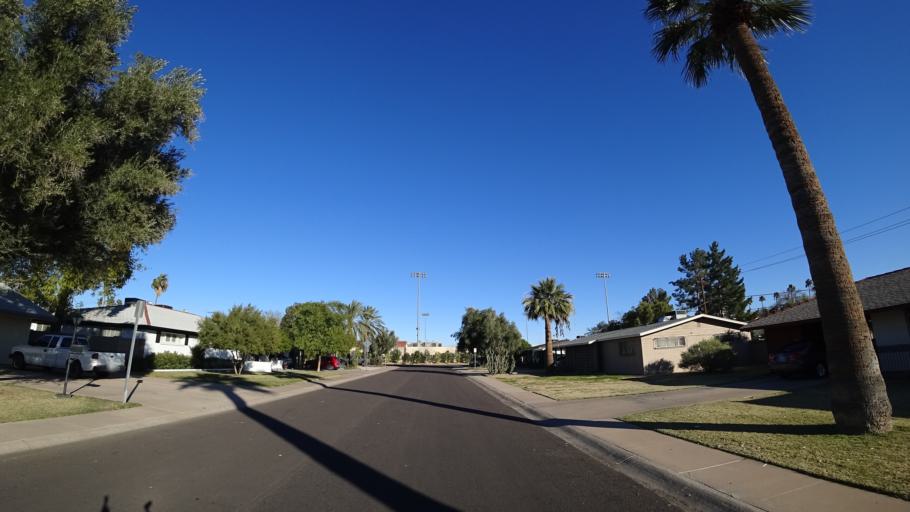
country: US
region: Arizona
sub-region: Maricopa County
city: Phoenix
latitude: 33.5067
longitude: -112.0680
